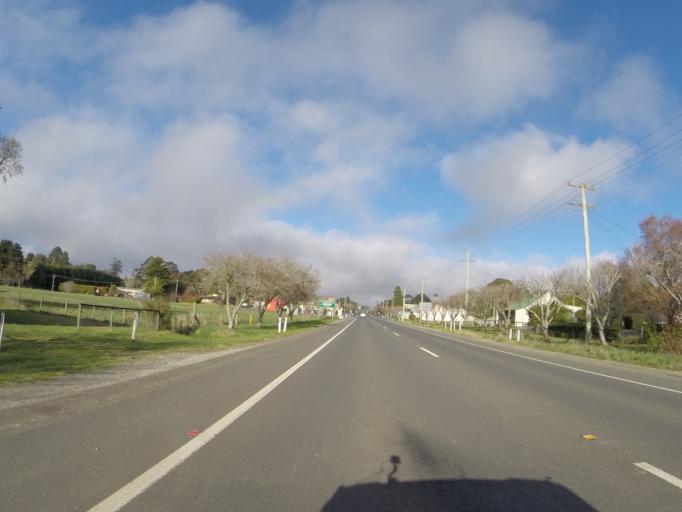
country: AU
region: New South Wales
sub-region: Shellharbour
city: Calderwood
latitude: -34.5878
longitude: 150.5879
